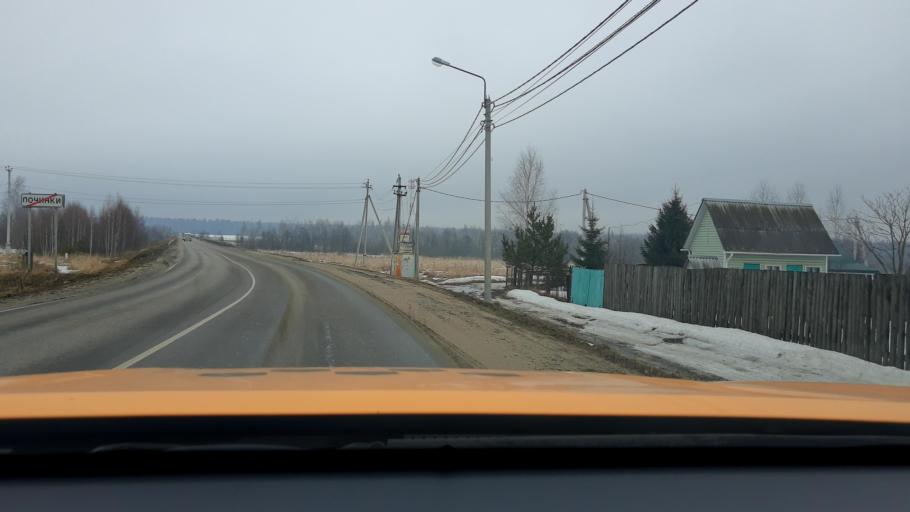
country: RU
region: Moskovskaya
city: Yamkino
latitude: 55.9178
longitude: 38.4441
